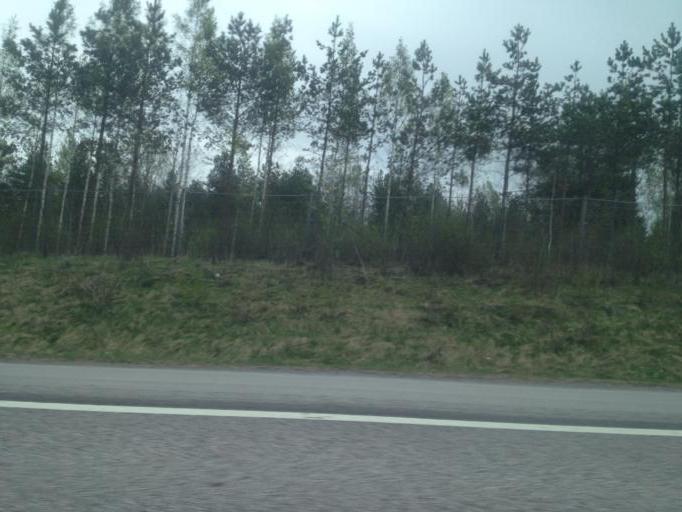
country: FI
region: Uusimaa
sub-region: Helsinki
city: Hyvinge
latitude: 60.6344
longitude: 24.8098
